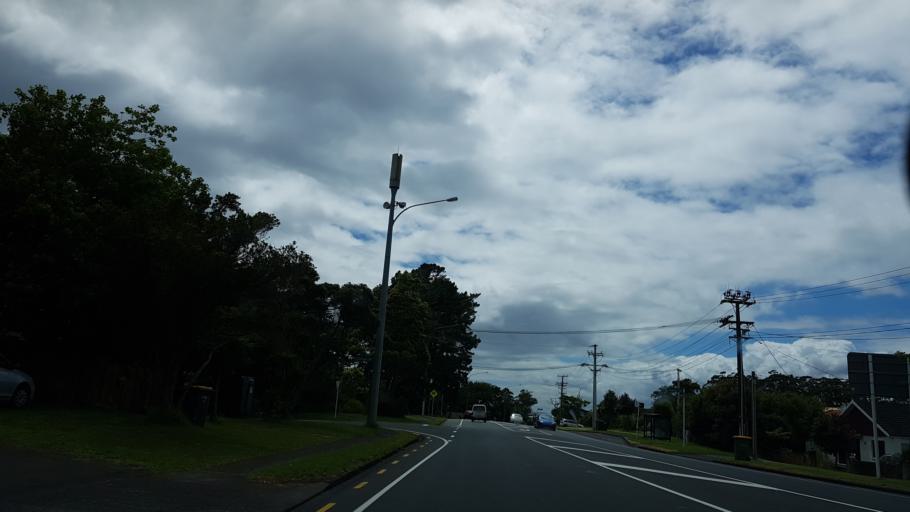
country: NZ
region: Auckland
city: Murrays Bay
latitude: -36.7471
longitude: 174.7422
